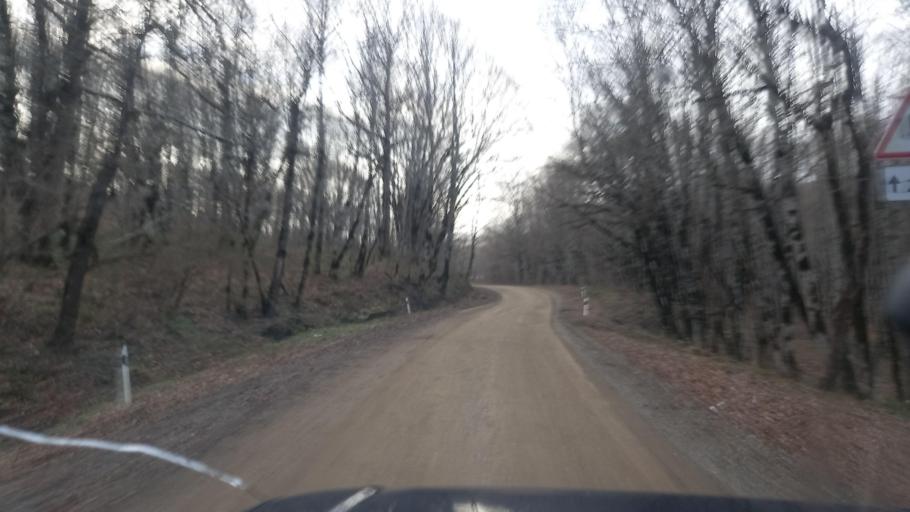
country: RU
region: Krasnodarskiy
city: Khadyzhensk
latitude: 44.3407
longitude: 39.2630
